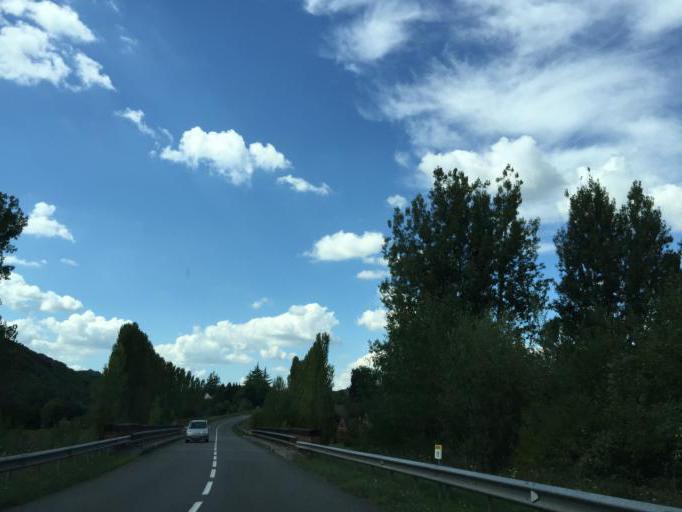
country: FR
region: Midi-Pyrenees
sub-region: Departement de l'Aveyron
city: Saint-Christophe-Vallon
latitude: 44.5144
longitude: 2.4315
